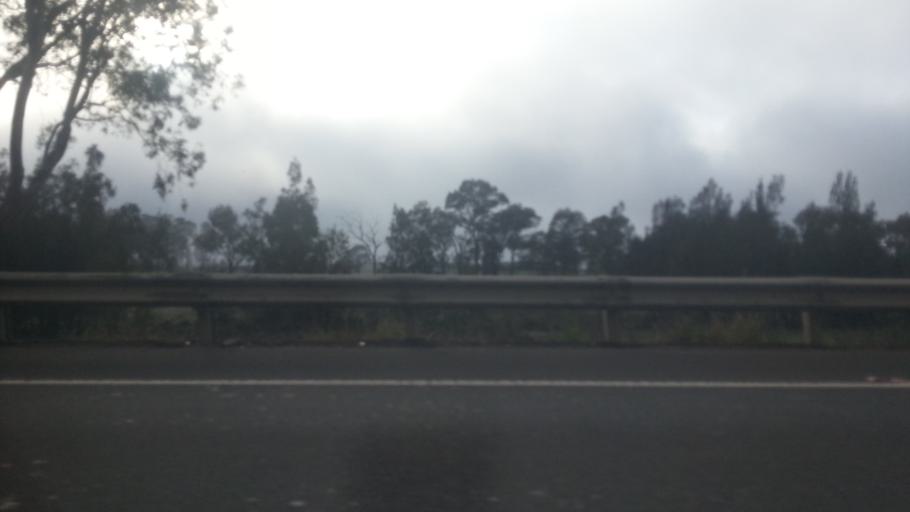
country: AU
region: New South Wales
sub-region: Penrith Municipality
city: Glenmore Park
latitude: -33.8092
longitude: 150.6947
